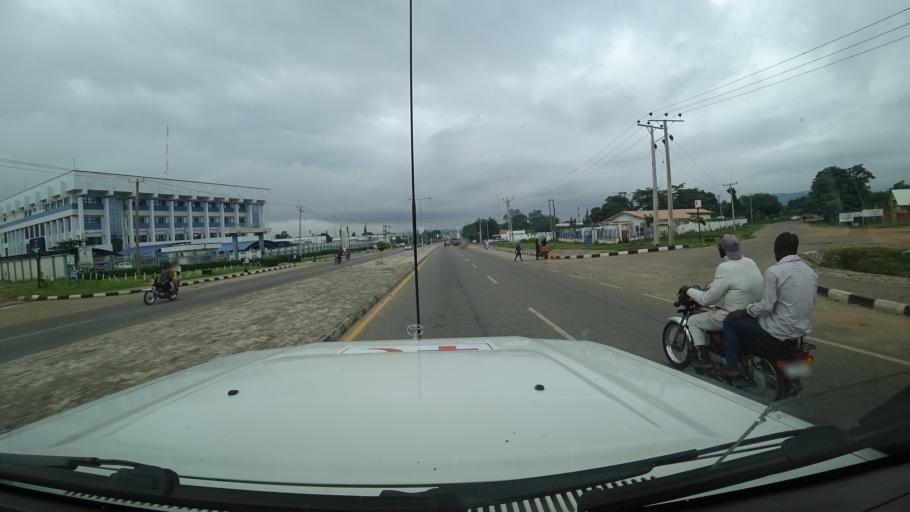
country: NG
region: Niger
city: Minna
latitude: 9.6085
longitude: 6.5531
